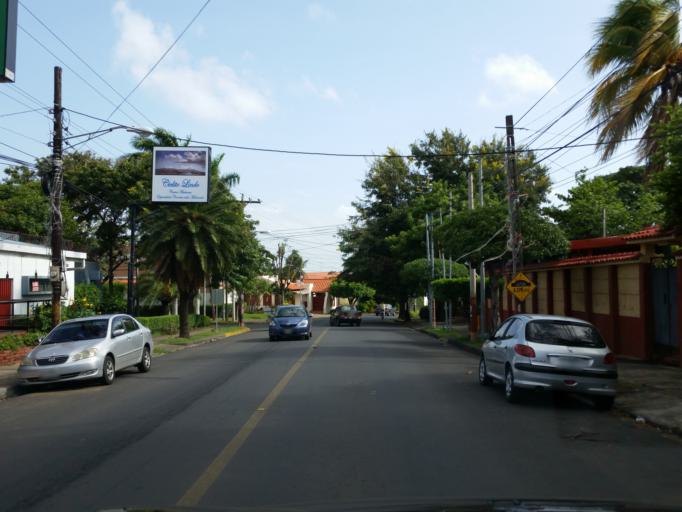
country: NI
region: Managua
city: Managua
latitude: 12.1211
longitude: -86.2664
